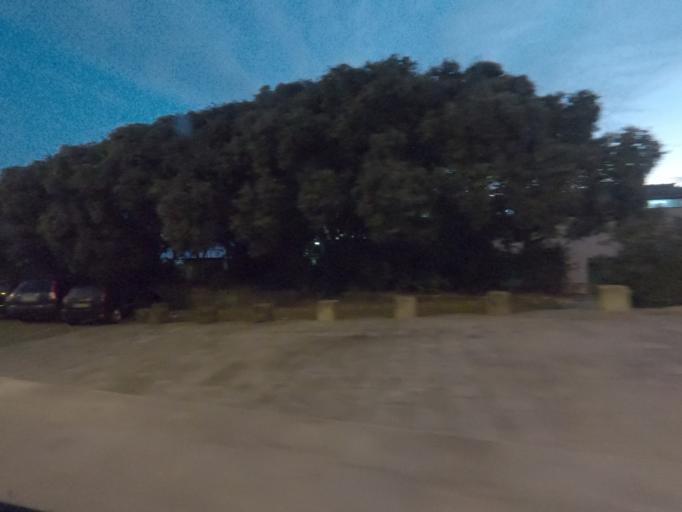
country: PT
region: Porto
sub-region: Vila Nova de Gaia
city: Canidelo
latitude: 41.1476
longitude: -8.6614
